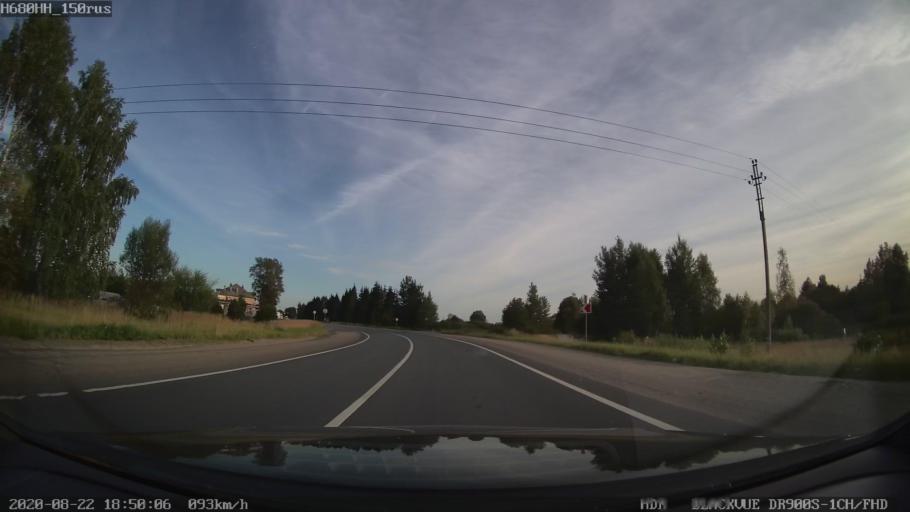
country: RU
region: Tverskaya
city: Rameshki
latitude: 57.2705
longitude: 36.0711
